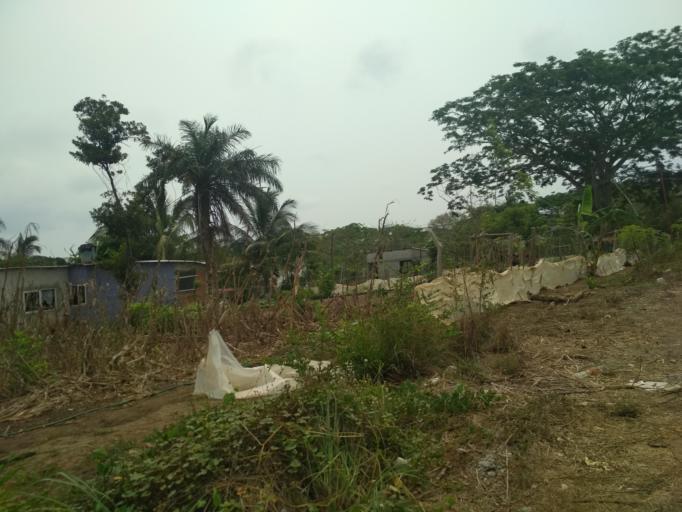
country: MX
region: Veracruz
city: Paso del Toro
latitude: 19.0218
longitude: -96.1381
